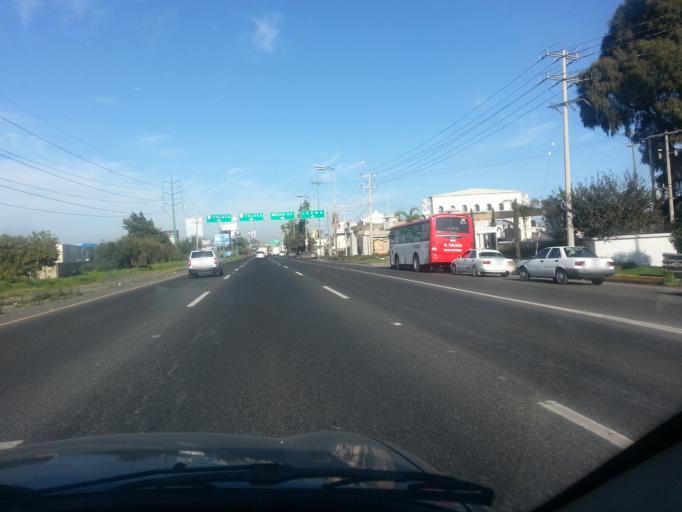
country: MX
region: Mexico
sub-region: Ocoyoacac
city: San Antonio el Llanito
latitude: 19.2842
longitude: -99.5000
